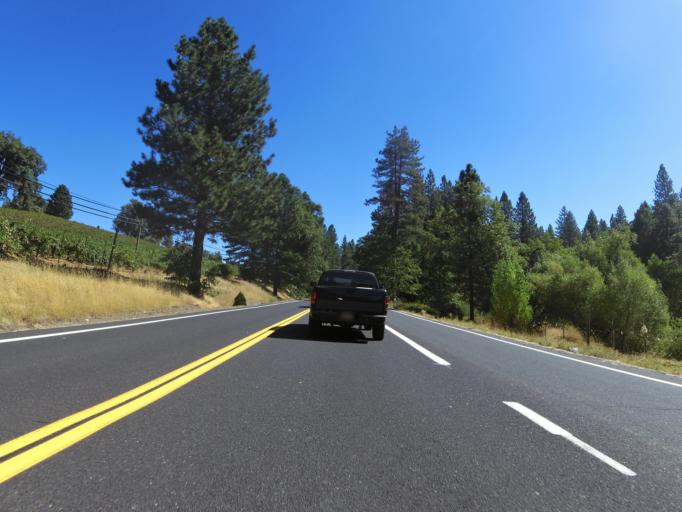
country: US
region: California
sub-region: Calaveras County
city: Forest Meadows
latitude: 38.1699
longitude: -120.4120
